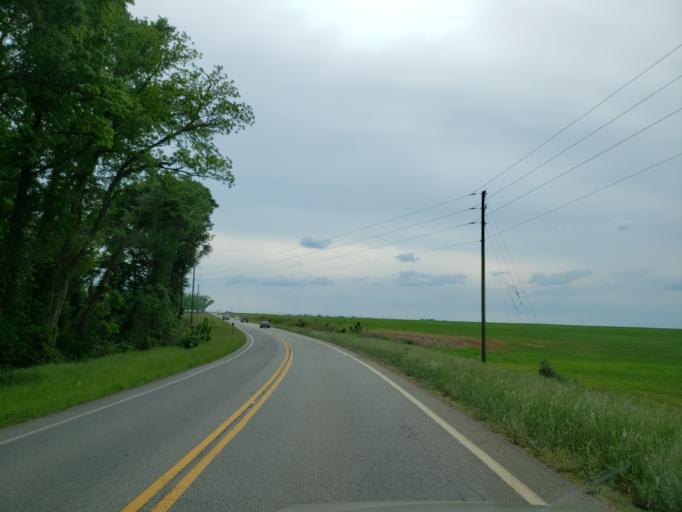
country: US
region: Georgia
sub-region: Macon County
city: Marshallville
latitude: 32.3663
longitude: -83.9161
